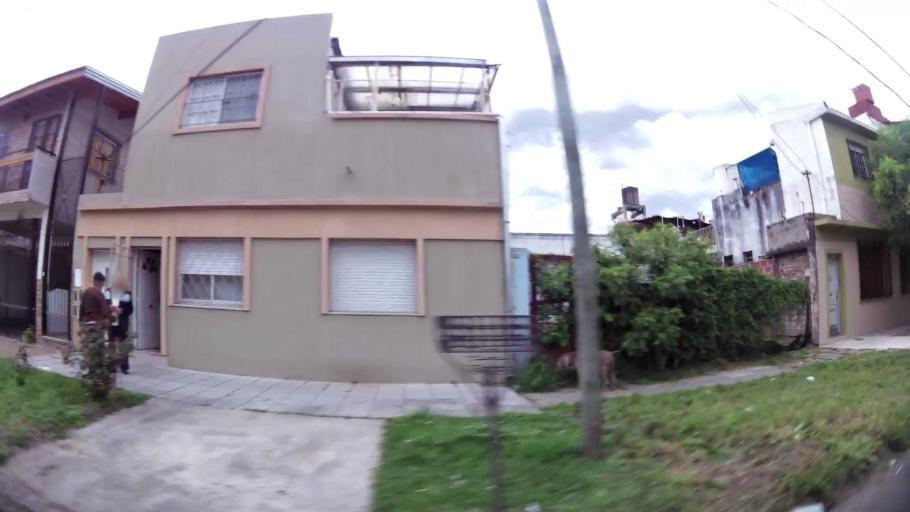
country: AR
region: Buenos Aires
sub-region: Partido de Lanus
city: Lanus
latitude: -34.6921
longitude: -58.3967
